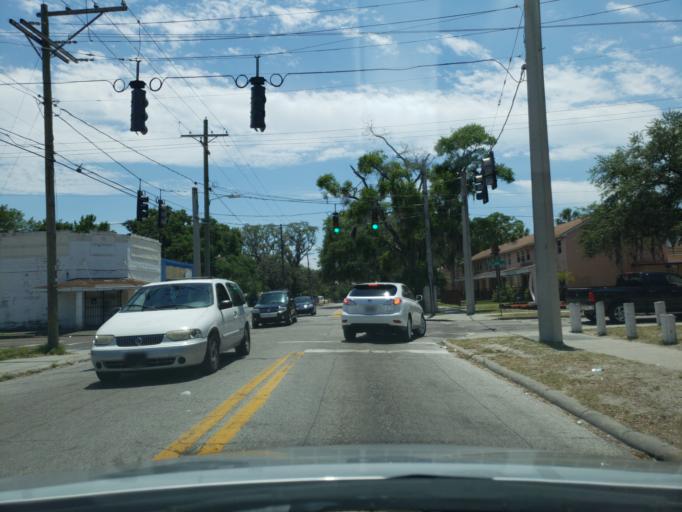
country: US
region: Florida
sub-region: Hillsborough County
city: Tampa
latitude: 27.9781
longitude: -82.4553
